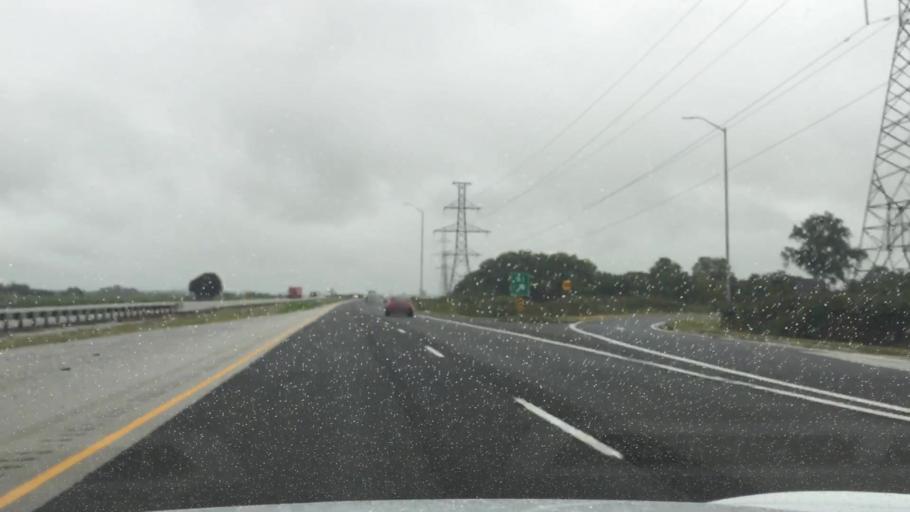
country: CA
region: Ontario
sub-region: Lambton County
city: Walpole Island
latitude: 42.3515
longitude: -82.1835
